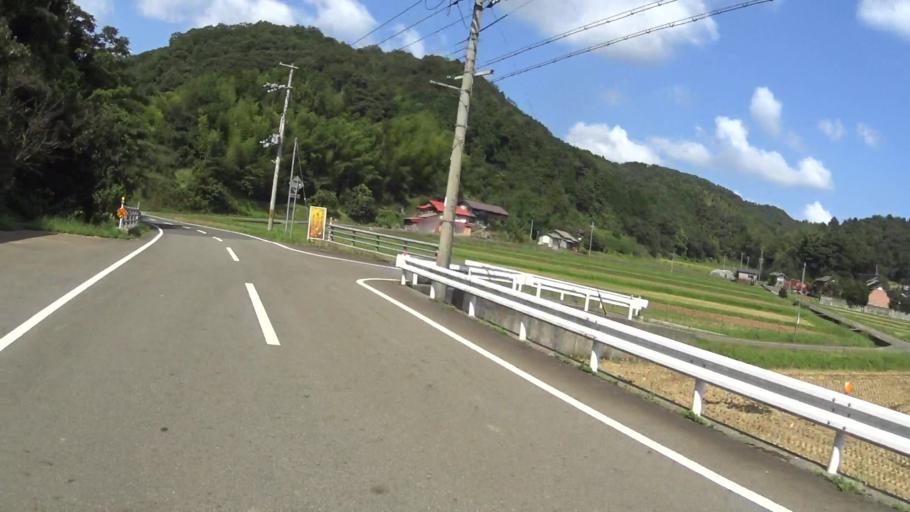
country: JP
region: Kyoto
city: Miyazu
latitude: 35.6827
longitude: 135.2666
